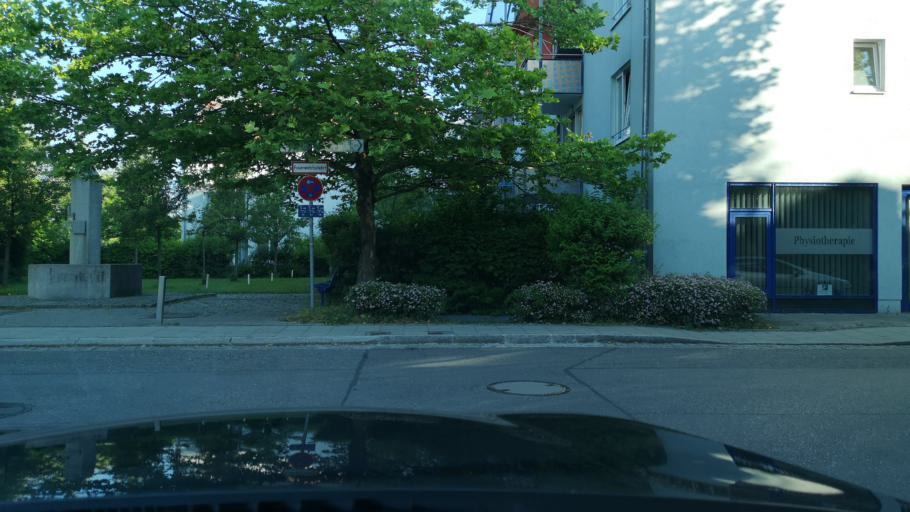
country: DE
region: Bavaria
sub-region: Upper Bavaria
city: Ismaning
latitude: 48.2210
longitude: 11.6631
